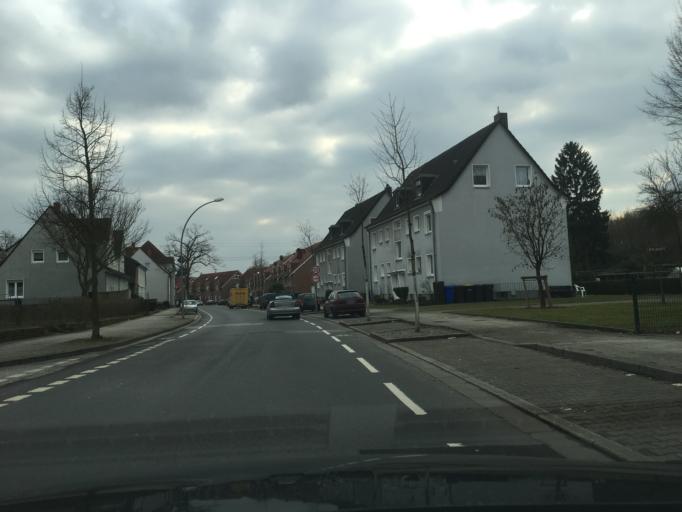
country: DE
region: North Rhine-Westphalia
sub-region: Regierungsbezirk Munster
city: Gladbeck
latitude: 51.5487
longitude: 7.0024
